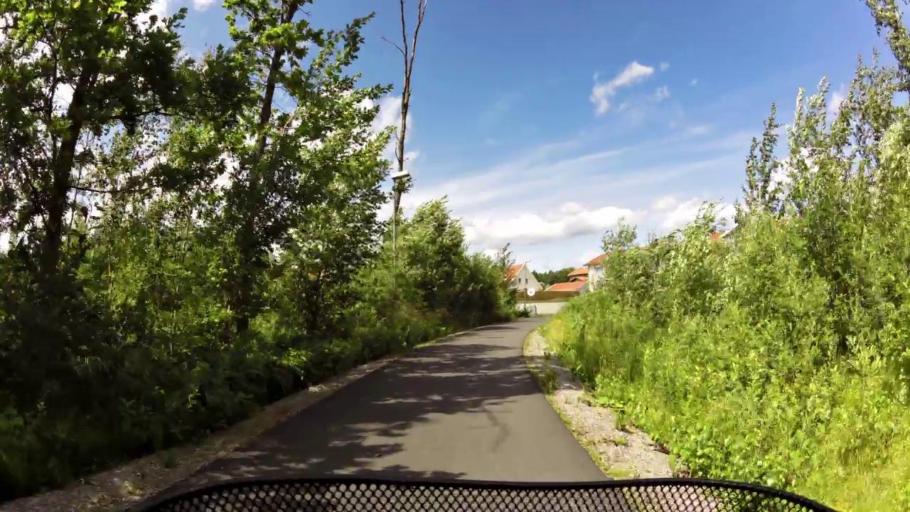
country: SE
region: OEstergoetland
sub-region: Linkopings Kommun
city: Ekangen
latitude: 58.4773
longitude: 15.6361
